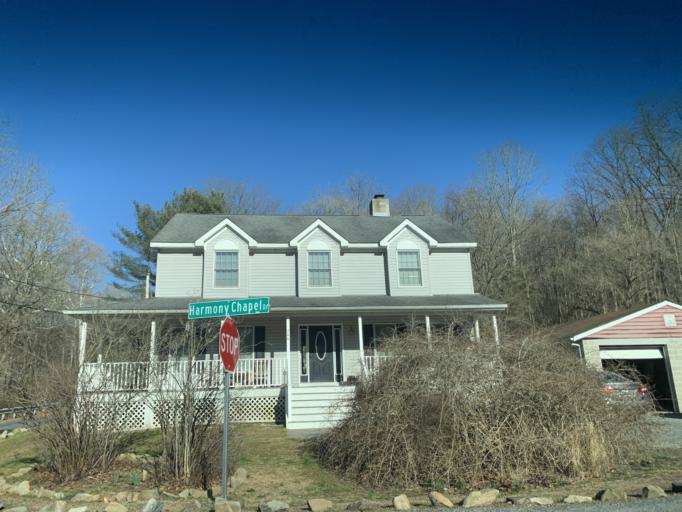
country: US
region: Maryland
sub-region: Cecil County
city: Rising Sun
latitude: 39.6553
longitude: -76.1367
